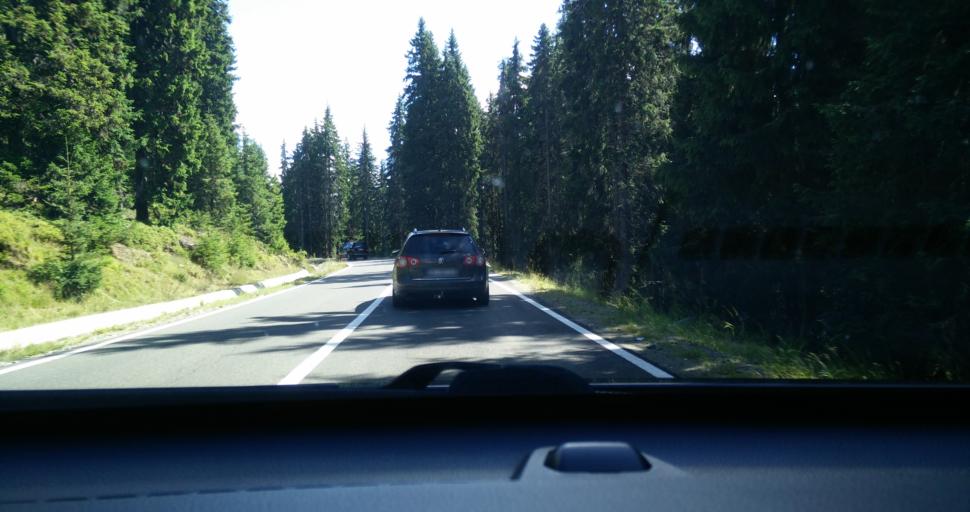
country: RO
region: Hunedoara
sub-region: Oras Petrila
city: Petrila
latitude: 45.4725
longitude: 23.6333
